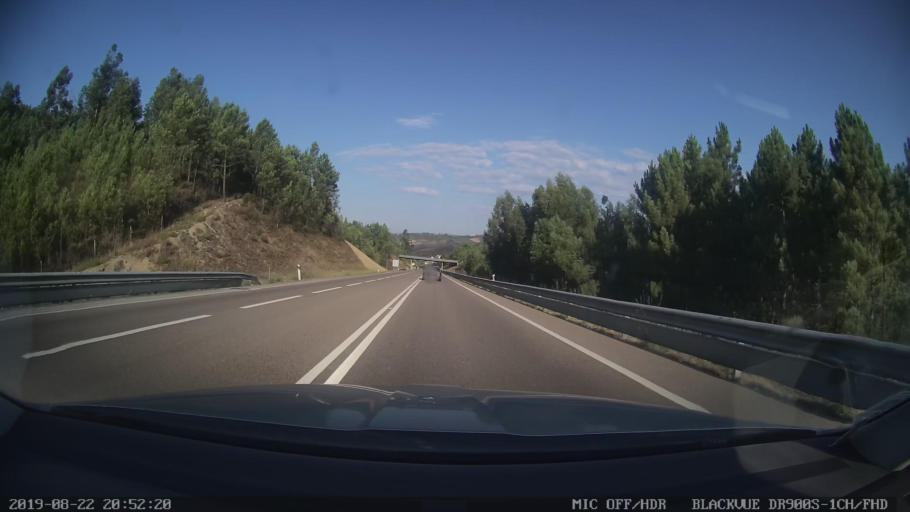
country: PT
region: Castelo Branco
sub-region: Proenca-A-Nova
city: Proenca-a-Nova
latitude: 39.7685
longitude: -7.9698
